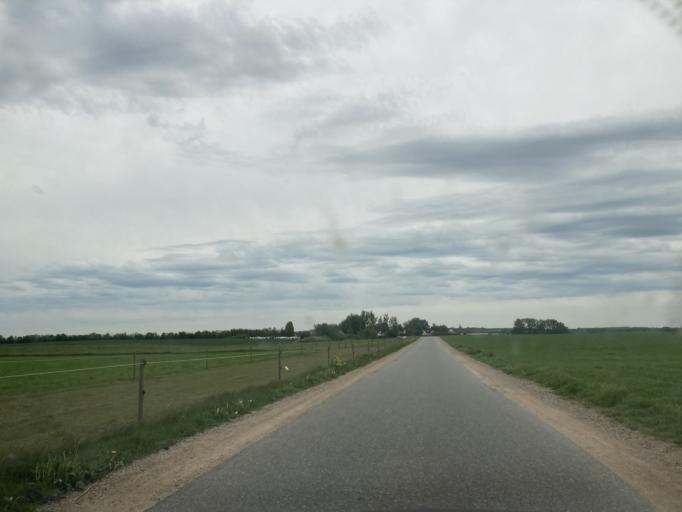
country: DK
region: Zealand
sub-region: Roskilde Kommune
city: Svogerslev
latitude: 55.6565
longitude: 11.9968
